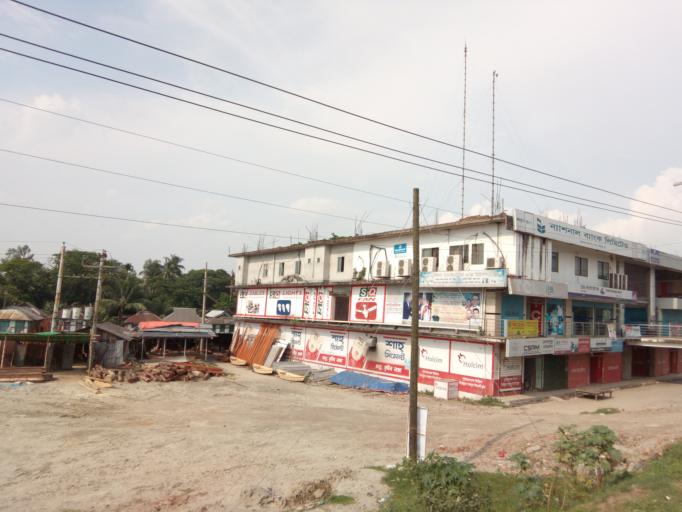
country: BD
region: Dhaka
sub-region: Dhaka
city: Dhaka
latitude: 23.6631
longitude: 90.3891
